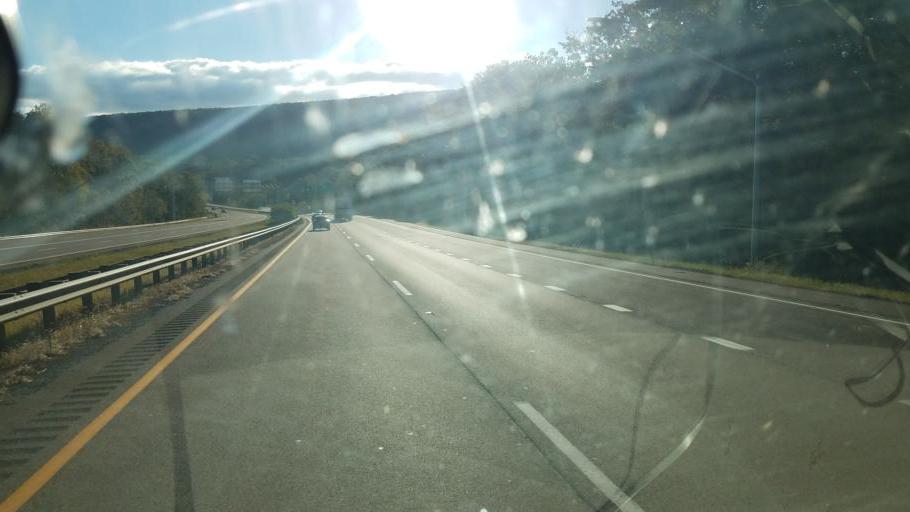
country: US
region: Maryland
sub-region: Allegany County
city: La Vale
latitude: 39.6353
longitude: -78.8363
